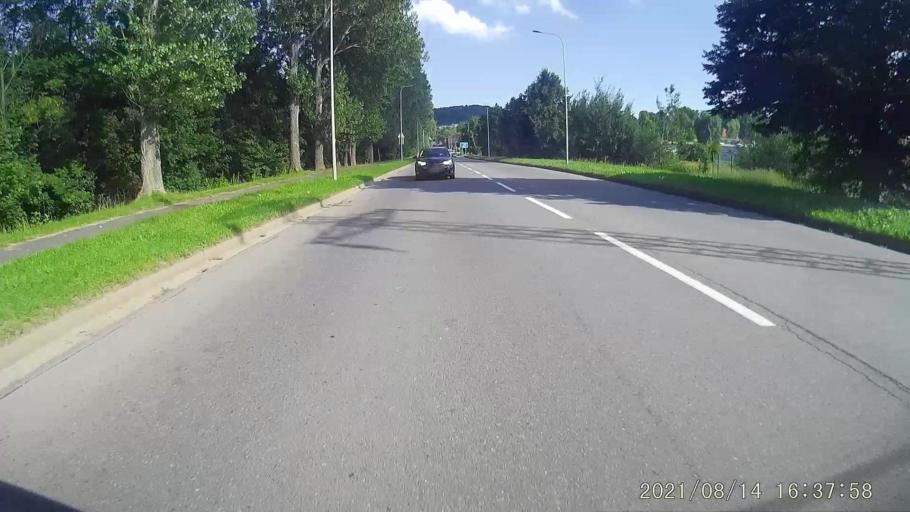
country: PL
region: Lower Silesian Voivodeship
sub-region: Powiat kamiennogorski
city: Kamienna Gora
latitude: 50.7890
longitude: 16.0365
